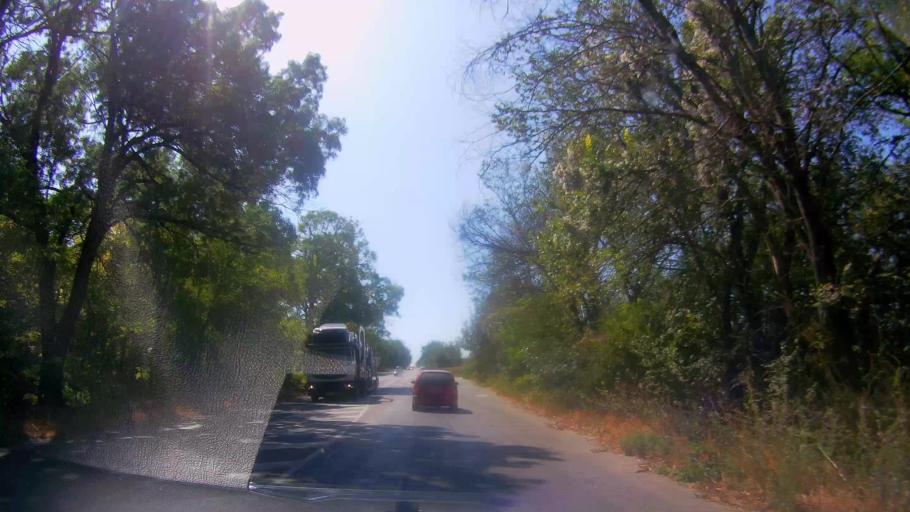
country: BG
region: Veliko Turnovo
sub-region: Obshtina Gorna Oryakhovitsa
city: Purvomaytsi
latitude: 43.2412
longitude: 25.6424
